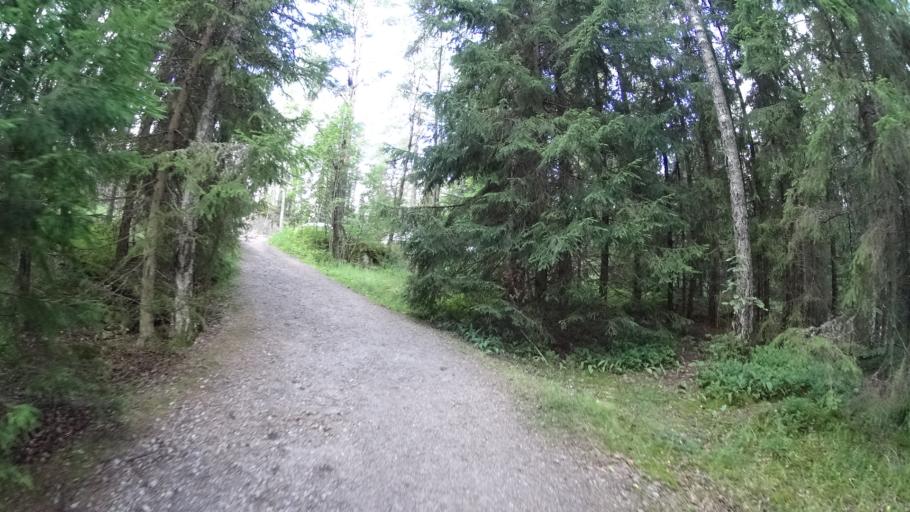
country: FI
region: Uusimaa
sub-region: Helsinki
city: Espoo
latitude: 60.3246
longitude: 24.6624
